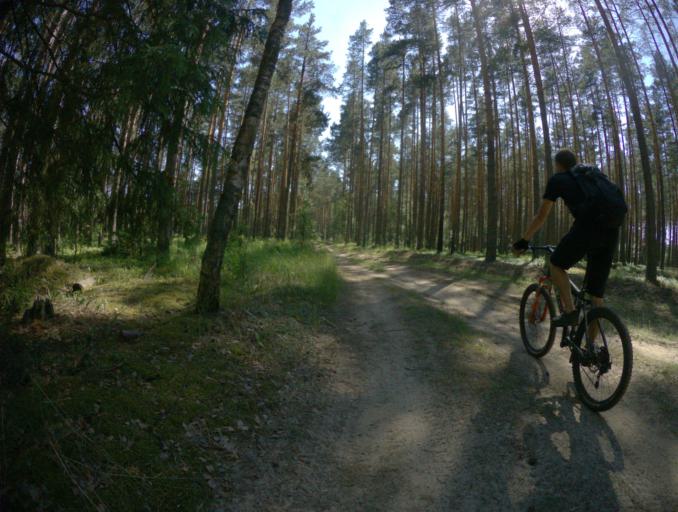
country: RU
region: Vladimir
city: Vyazniki
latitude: 56.3840
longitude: 42.2044
